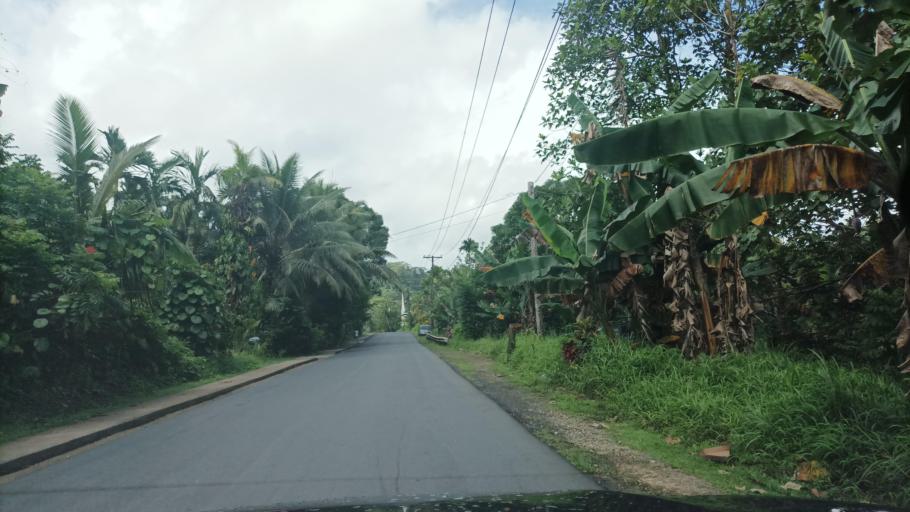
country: FM
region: Pohnpei
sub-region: Sokehs Municipality
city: Palikir - National Government Center
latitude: 6.9353
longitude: 158.1818
